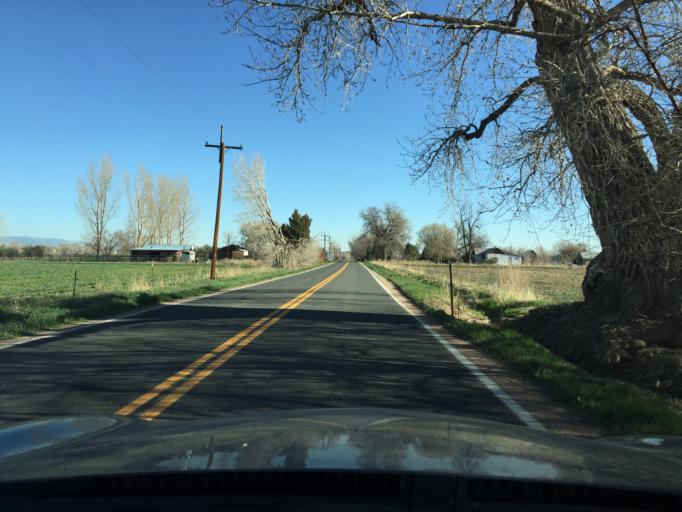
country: US
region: Colorado
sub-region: Boulder County
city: Erie
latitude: 40.0587
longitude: -105.0744
